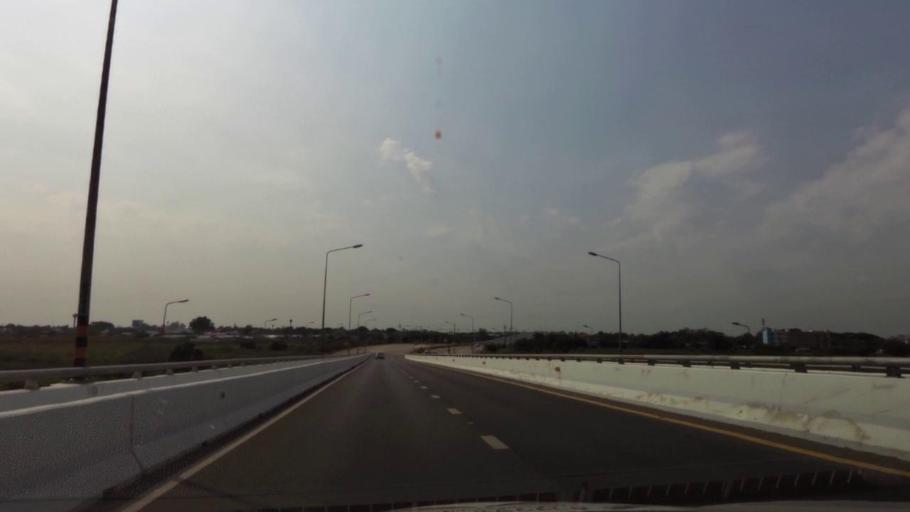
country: TH
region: Phra Nakhon Si Ayutthaya
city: Phra Nakhon Si Ayutthaya
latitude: 14.3296
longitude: 100.5823
